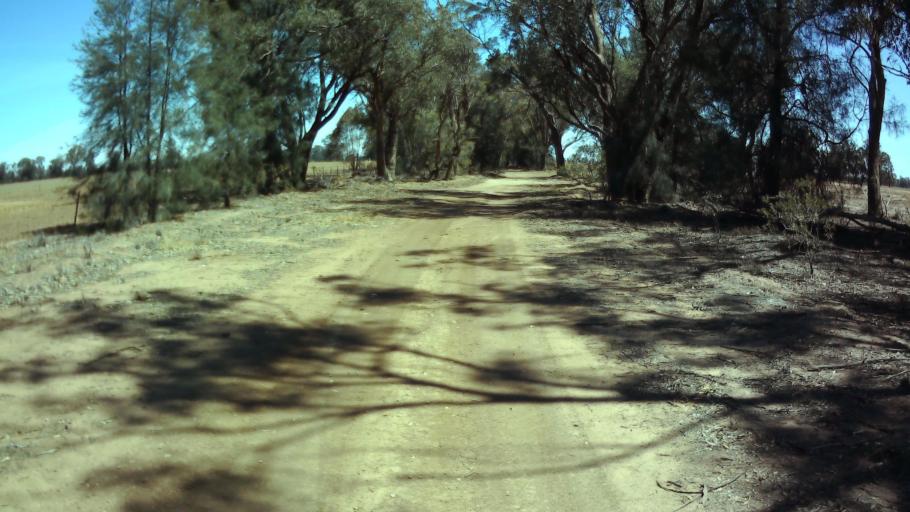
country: AU
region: New South Wales
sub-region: Bland
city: West Wyalong
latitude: -33.9134
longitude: 147.6841
